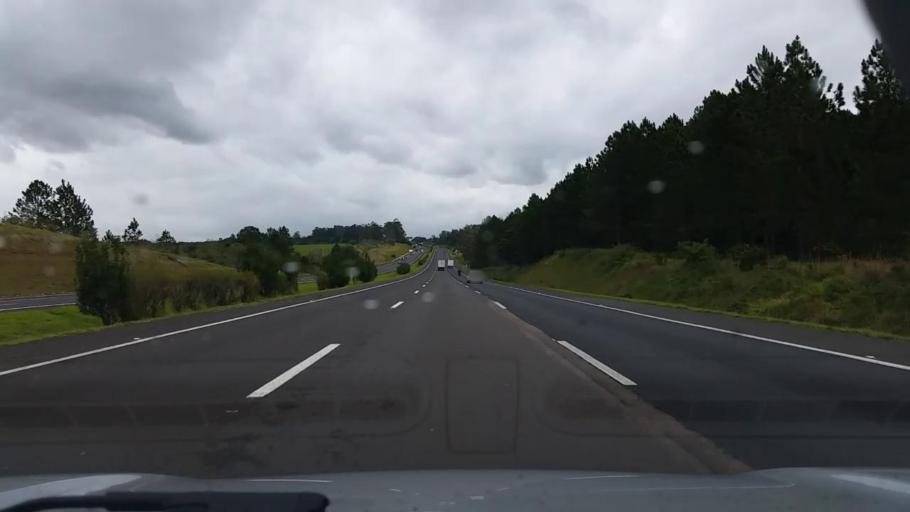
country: BR
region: Rio Grande do Sul
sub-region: Gravatai
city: Gravatai
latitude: -29.9259
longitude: -50.8626
